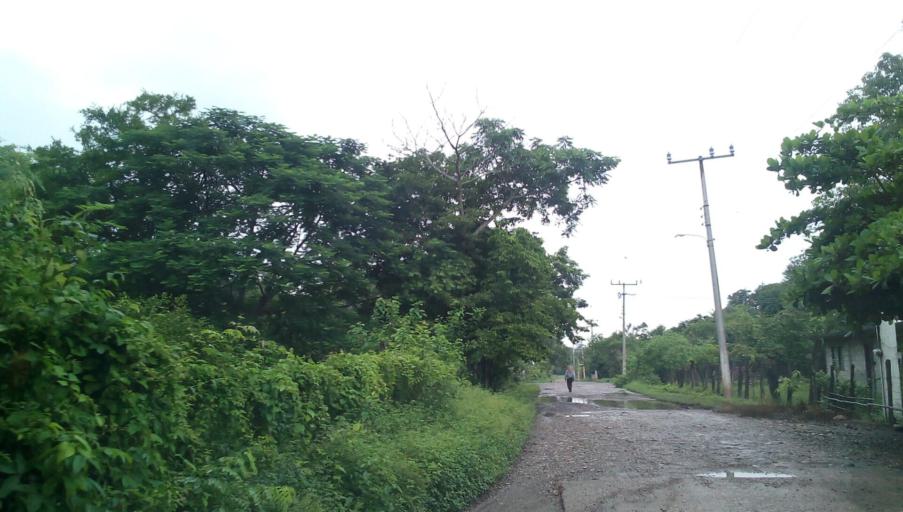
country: MX
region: Veracruz
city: Tempoal de Sanchez
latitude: 21.4189
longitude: -98.4253
